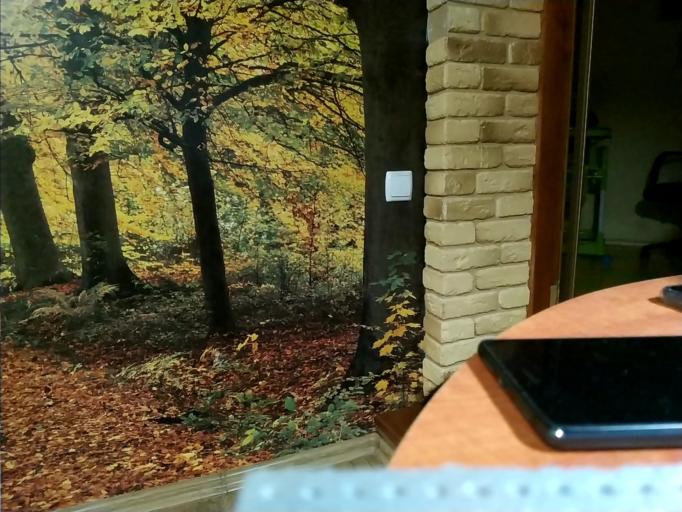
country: RU
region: Tverskaya
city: Zubtsov
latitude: 56.2894
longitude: 34.6878
